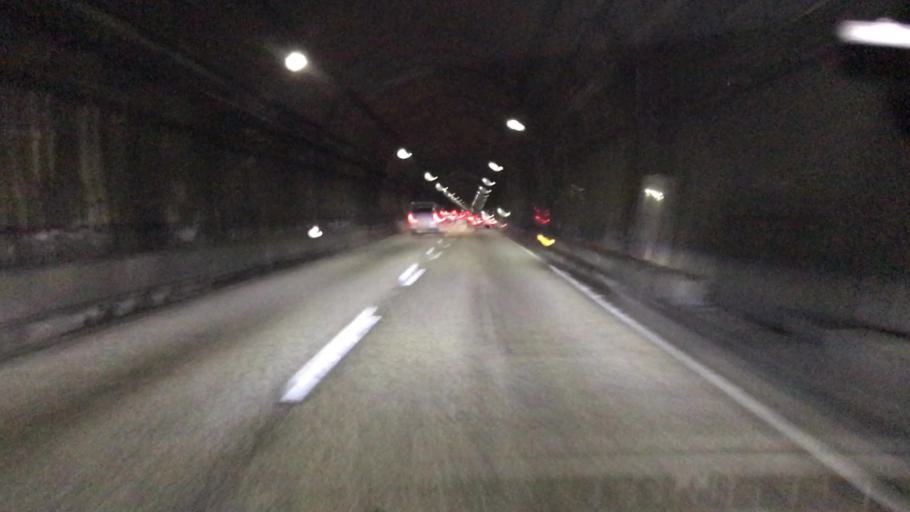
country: JP
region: Hyogo
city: Kobe
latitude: 34.7287
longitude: 135.1806
